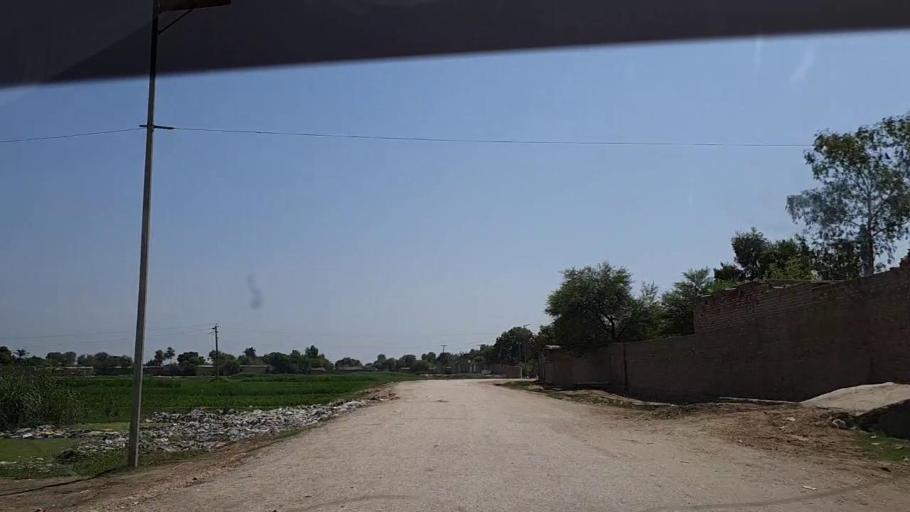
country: PK
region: Sindh
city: Ghauspur
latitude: 28.1417
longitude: 69.0879
